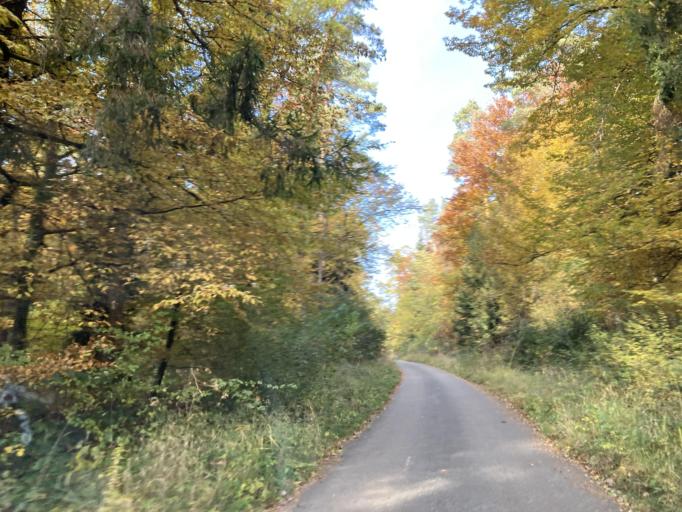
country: DE
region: Baden-Wuerttemberg
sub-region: Tuebingen Region
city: Bodelshausen
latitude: 48.4082
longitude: 8.9633
